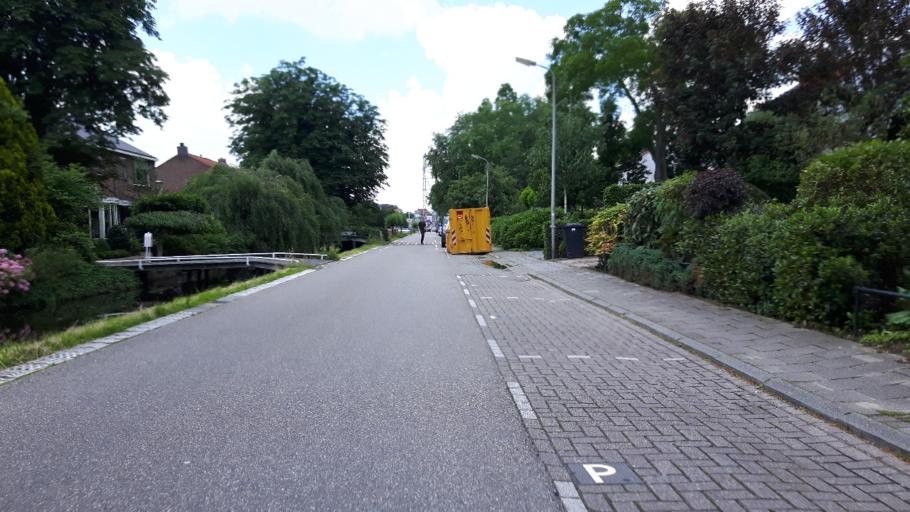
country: NL
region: South Holland
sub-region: Gemeente Waddinxveen
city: Oranjewijk
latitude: 52.0441
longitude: 4.6665
